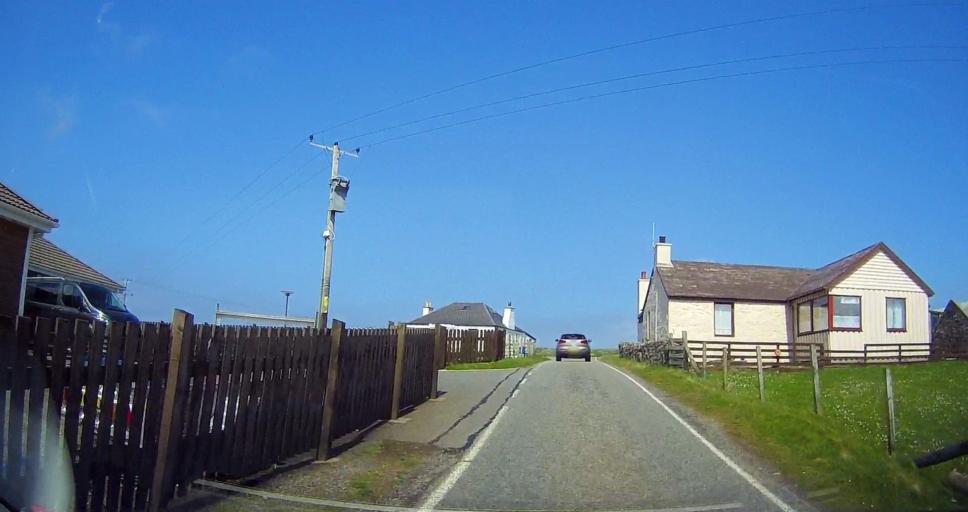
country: GB
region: Scotland
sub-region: Shetland Islands
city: Sandwick
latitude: 60.0834
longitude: -1.3320
